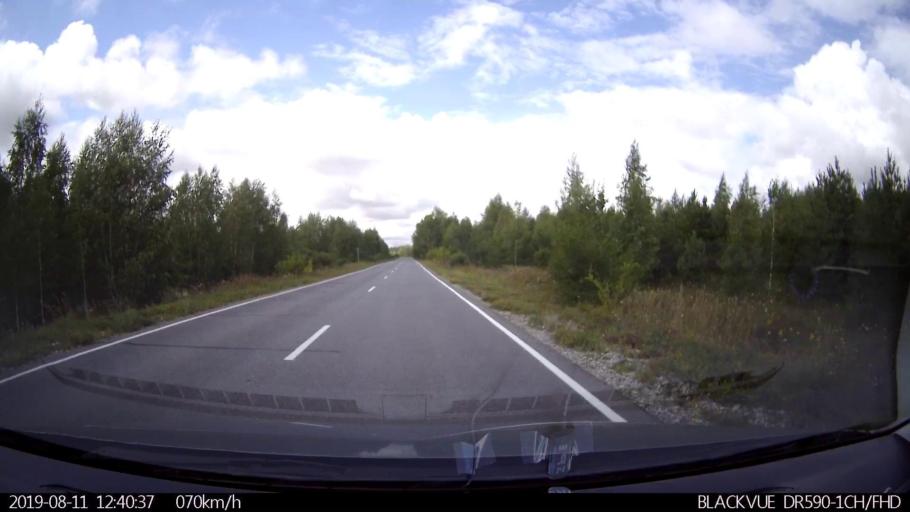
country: RU
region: Ulyanovsk
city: Ignatovka
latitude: 53.8398
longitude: 47.7779
